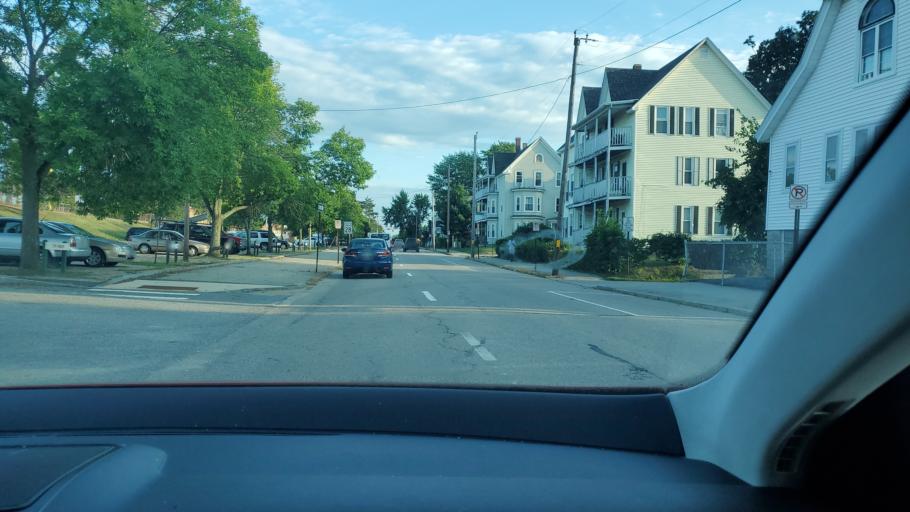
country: US
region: New Hampshire
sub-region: Hillsborough County
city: Manchester
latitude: 42.9834
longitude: -71.4553
